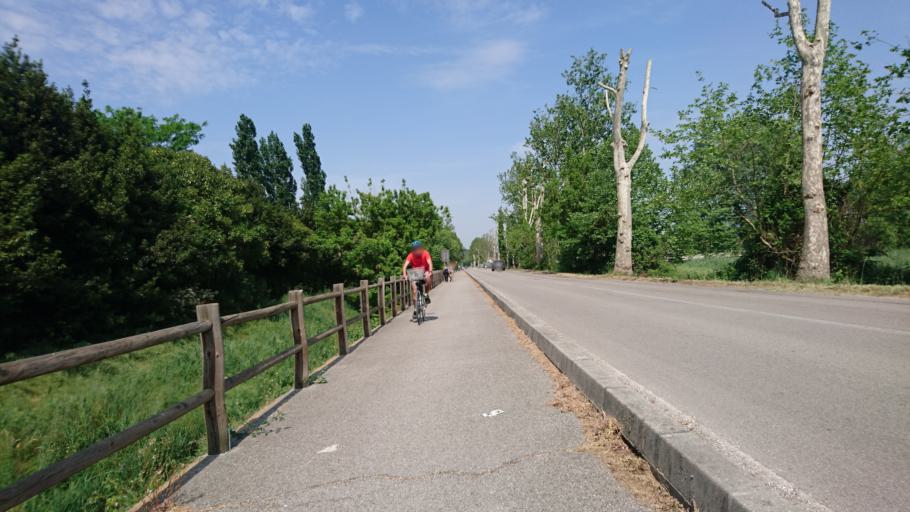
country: IT
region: Veneto
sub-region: Provincia di Padova
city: Battaglia Terme
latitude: 45.2872
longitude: 11.7672
